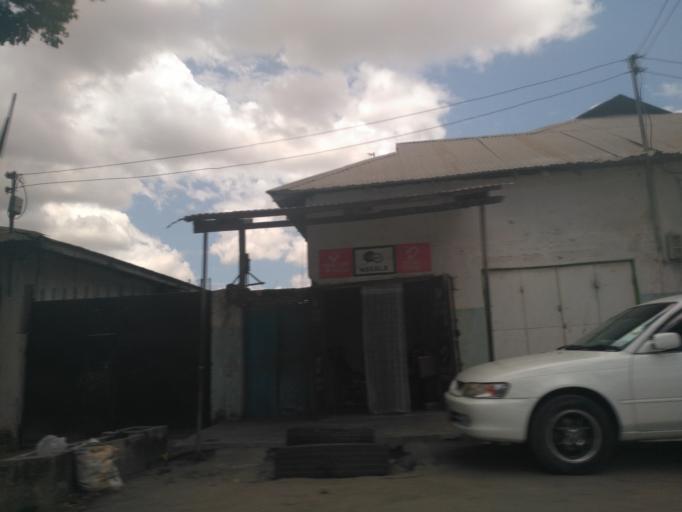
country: TZ
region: Dar es Salaam
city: Dar es Salaam
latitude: -6.8666
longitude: 39.2692
